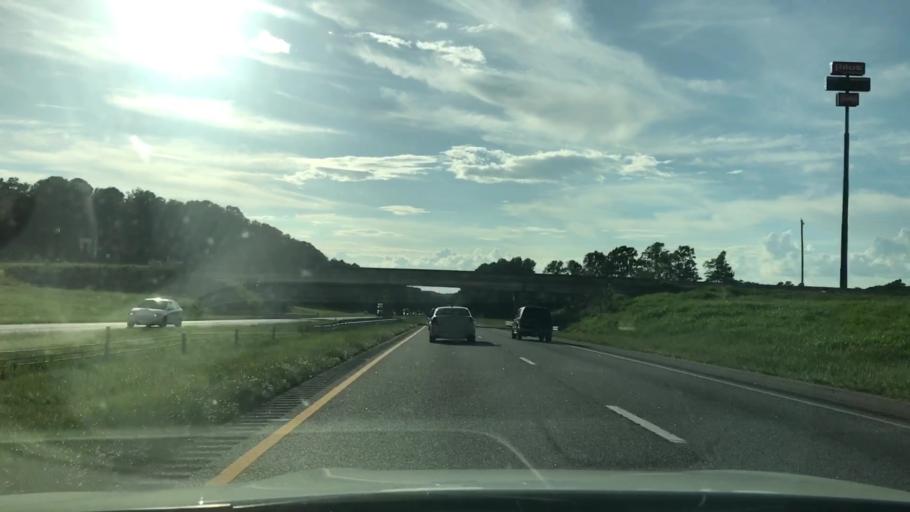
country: US
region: South Carolina
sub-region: Newberry County
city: Prosperity
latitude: 34.2387
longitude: -81.4593
